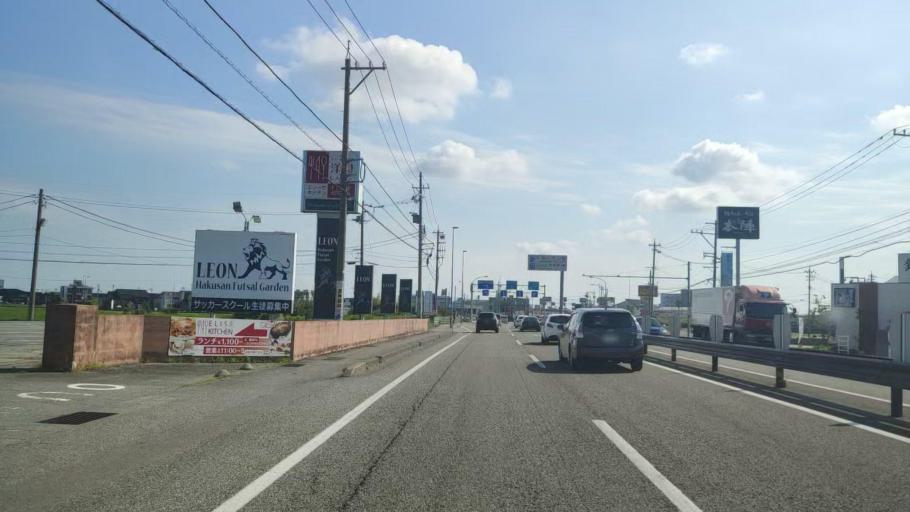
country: JP
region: Ishikawa
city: Matsuto
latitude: 36.5232
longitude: 136.5820
